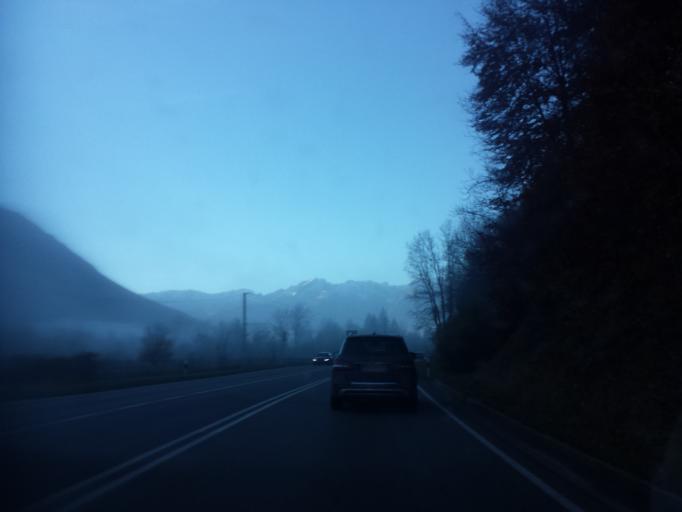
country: DE
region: Bavaria
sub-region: Upper Bavaria
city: Oberau
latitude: 47.5550
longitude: 11.1364
